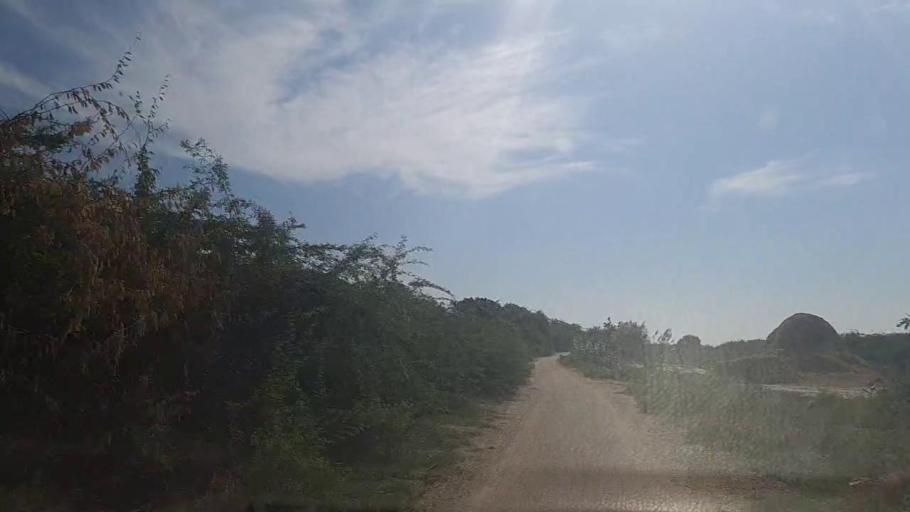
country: PK
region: Sindh
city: Mirpur Batoro
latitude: 24.6663
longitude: 68.1848
